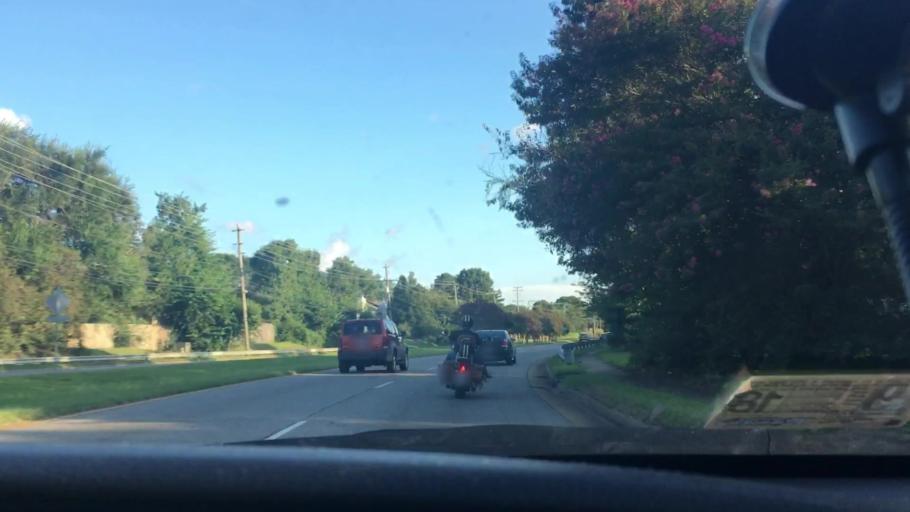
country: US
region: Virginia
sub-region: City of Chesapeake
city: Chesapeake
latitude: 36.8820
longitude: -76.1332
